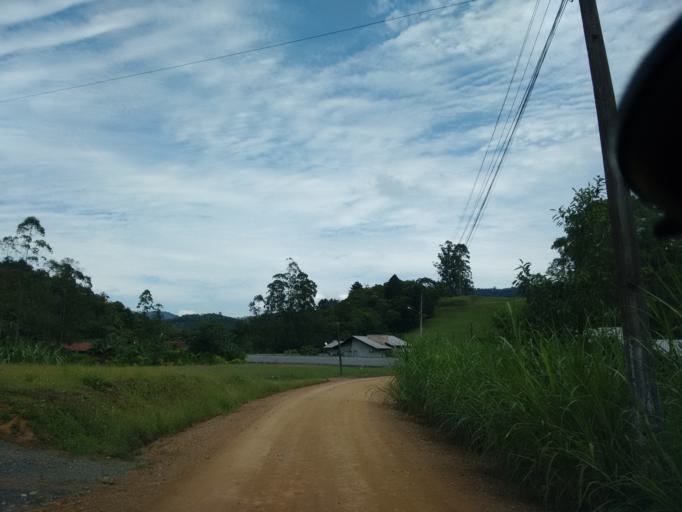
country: BR
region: Santa Catarina
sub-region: Pomerode
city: Pomerode
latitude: -26.8081
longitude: -49.1575
